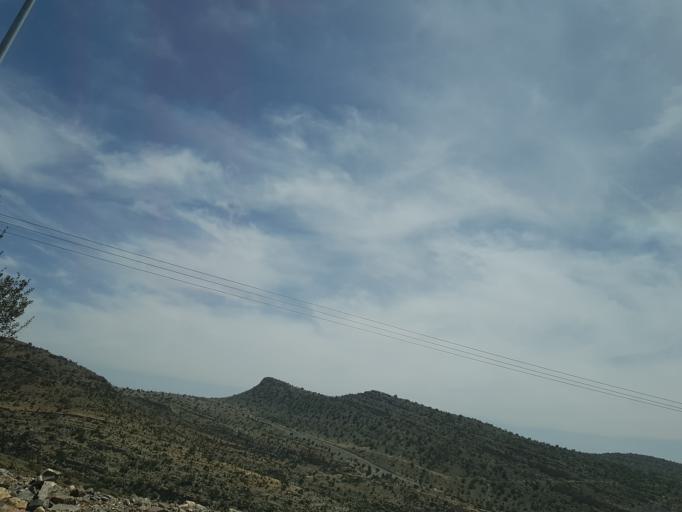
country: OM
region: Al Batinah
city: Bayt al `Awabi
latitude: 23.1349
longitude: 57.5690
